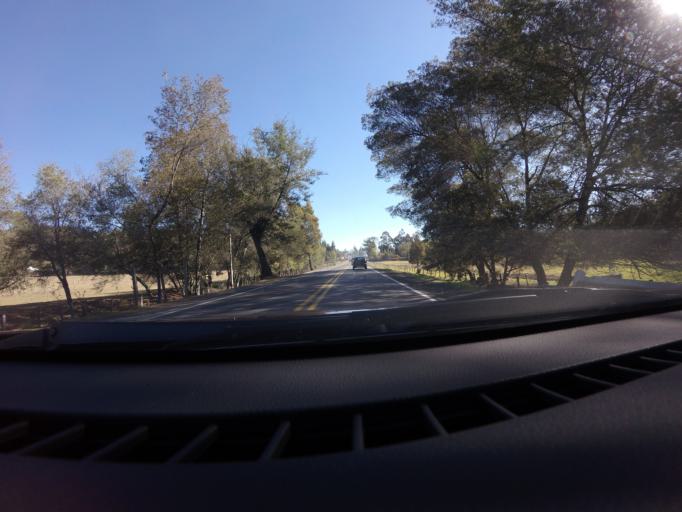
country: CO
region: Cundinamarca
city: Sutatausa
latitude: 5.2749
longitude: -73.8308
